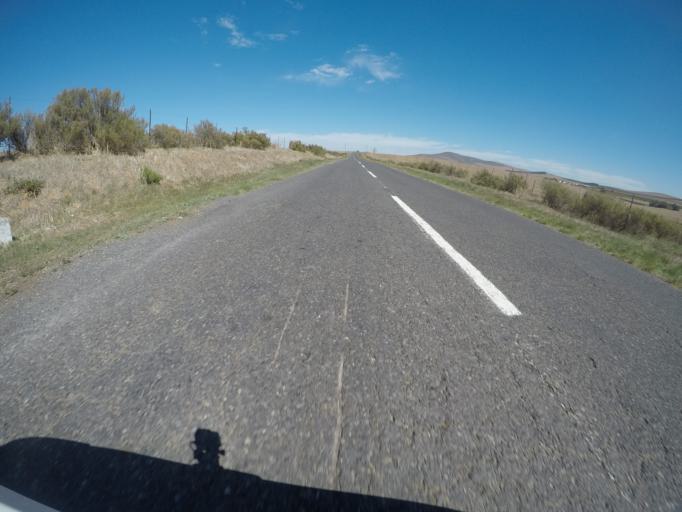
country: ZA
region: Western Cape
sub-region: City of Cape Town
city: Atlantis
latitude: -33.6814
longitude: 18.6023
